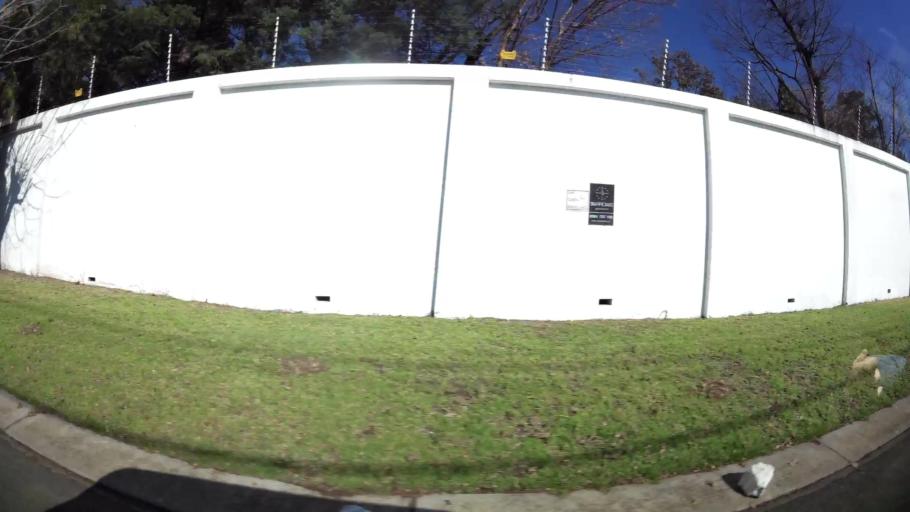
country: ZA
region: Gauteng
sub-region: City of Johannesburg Metropolitan Municipality
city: Midrand
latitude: -26.0484
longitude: 28.0492
